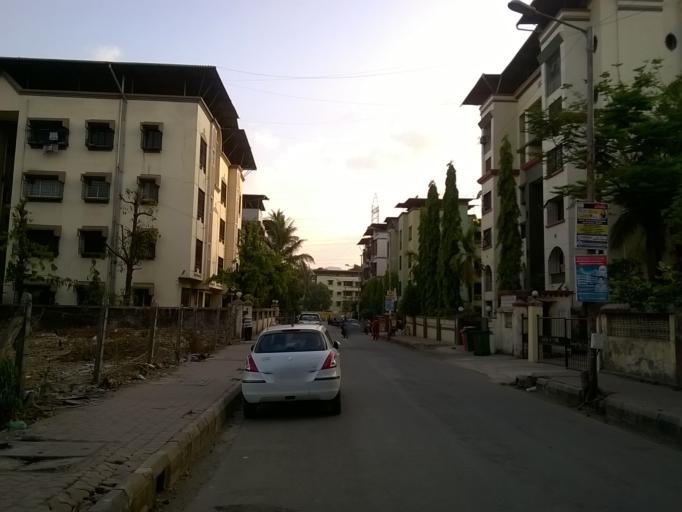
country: IN
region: Maharashtra
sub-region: Raigarh
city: Kalundri
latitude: 18.9912
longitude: 73.1259
